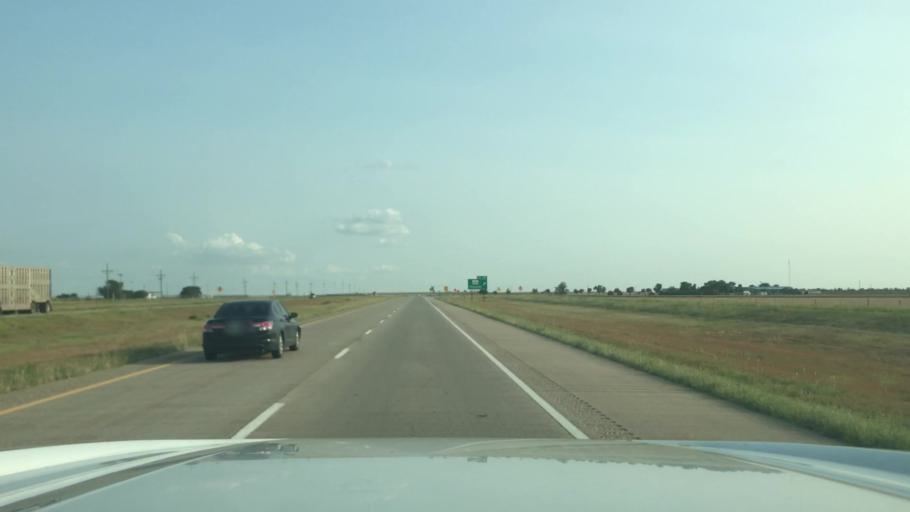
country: US
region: Texas
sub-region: Randall County
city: Canyon
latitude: 34.8175
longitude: -101.8488
